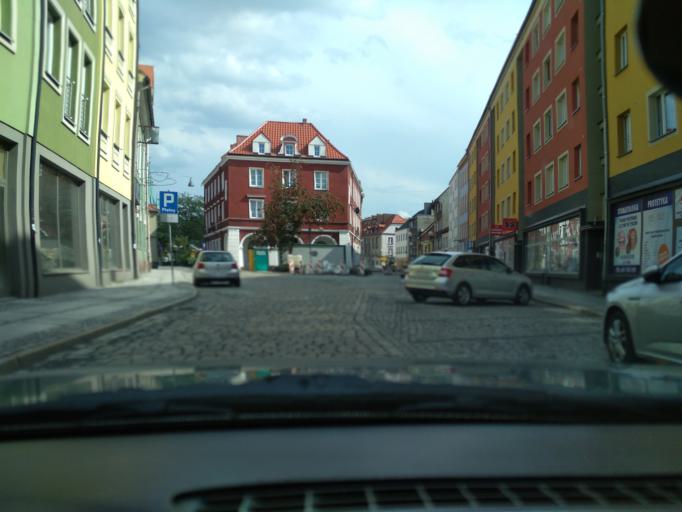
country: PL
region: Silesian Voivodeship
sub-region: Powiat raciborski
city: Raciborz
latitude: 50.0933
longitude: 18.2158
